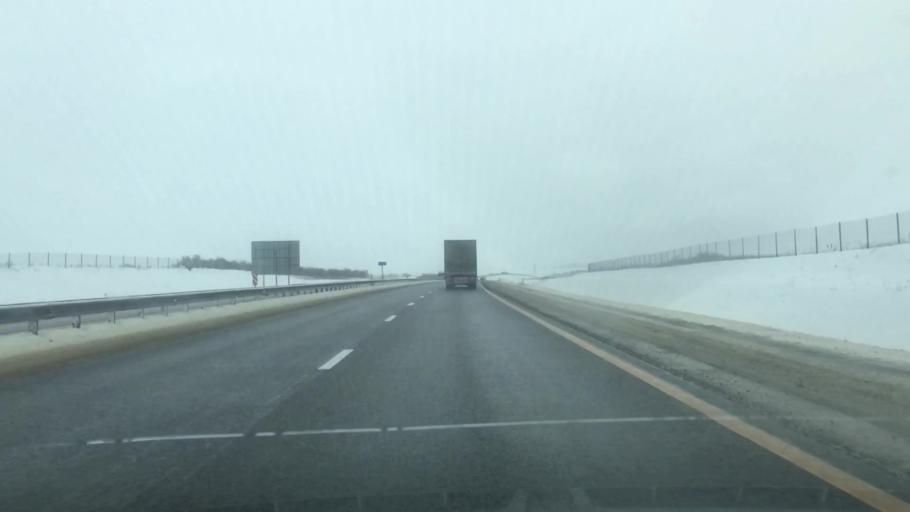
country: RU
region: Tula
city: Yefremov
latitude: 53.1535
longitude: 38.2503
